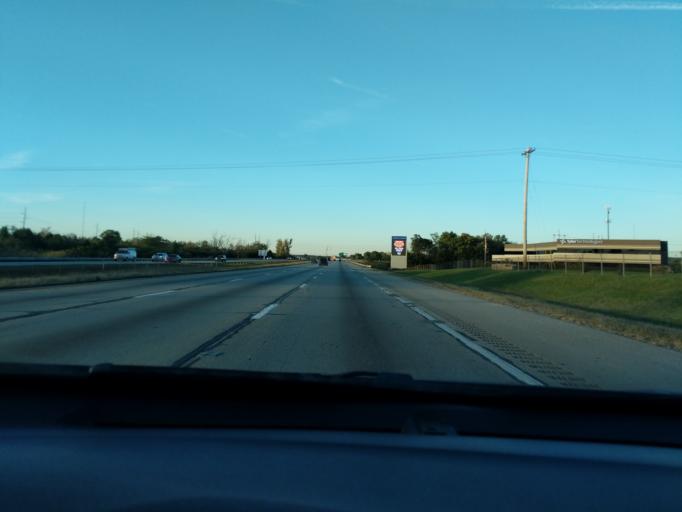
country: US
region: Ohio
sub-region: Montgomery County
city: Moraine
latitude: 39.6971
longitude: -84.2294
